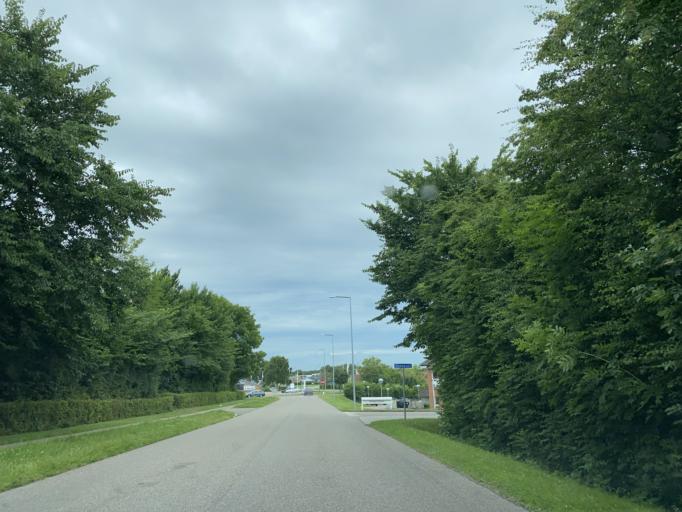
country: DK
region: South Denmark
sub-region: Sonderborg Kommune
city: Sonderborg
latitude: 54.9224
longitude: 9.7998
